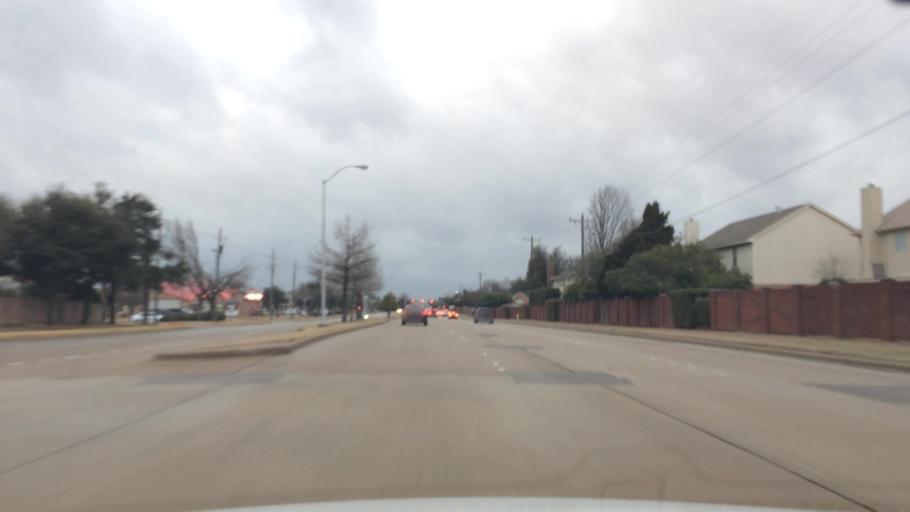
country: US
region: Texas
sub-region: Collin County
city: Frisco
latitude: 33.0894
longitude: -96.7717
